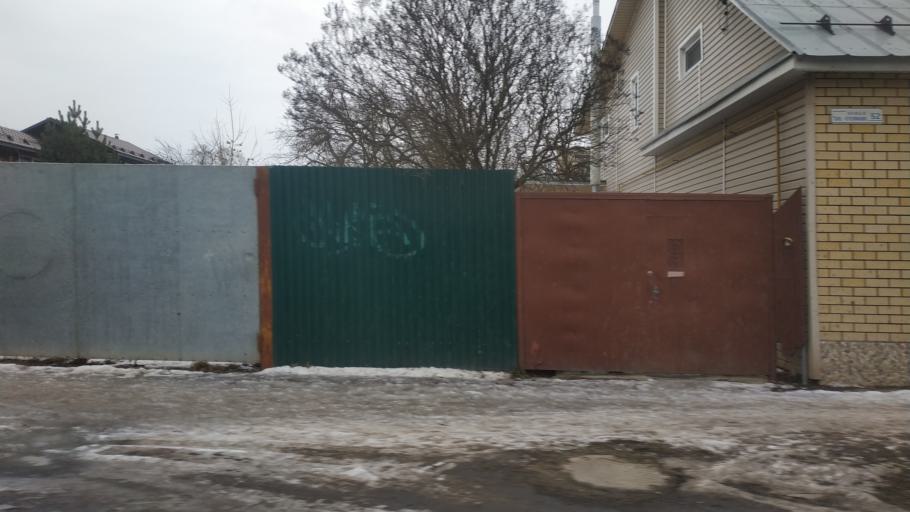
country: RU
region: Tverskaya
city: Tver
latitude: 56.8779
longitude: 35.8926
